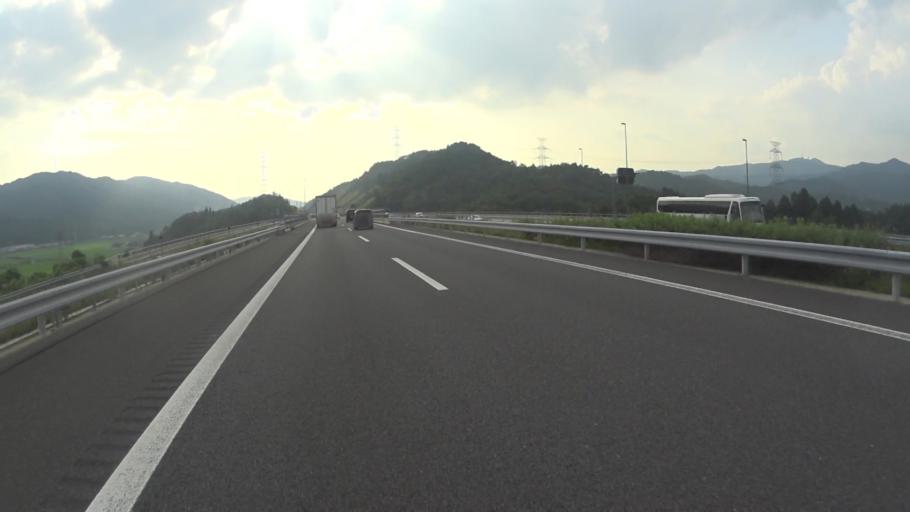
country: JP
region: Shiga Prefecture
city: Minakuchicho-matoba
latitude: 34.9255
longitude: 136.0846
